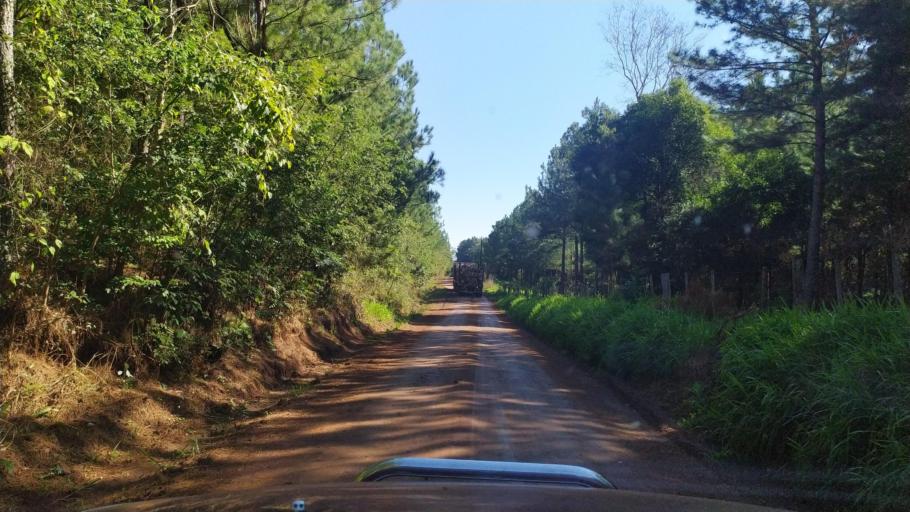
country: AR
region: Misiones
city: El Alcazar
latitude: -26.7372
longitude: -54.6456
